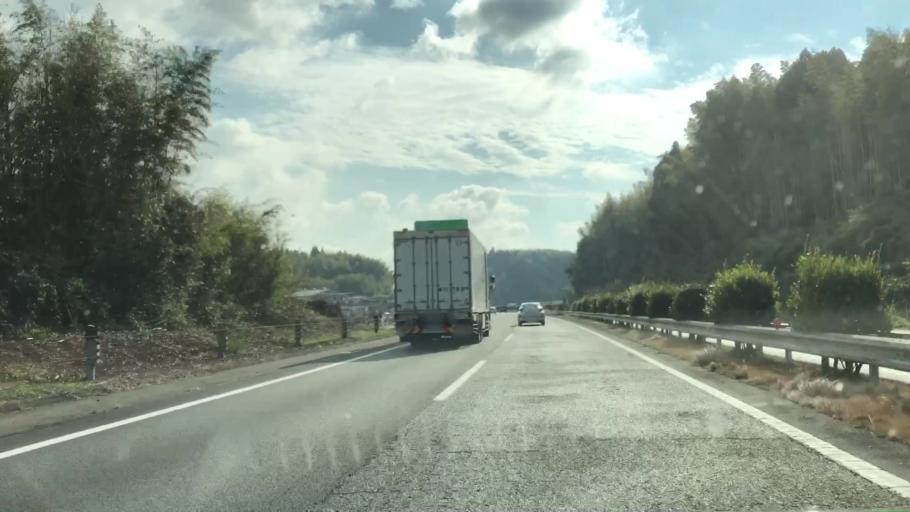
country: JP
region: Fukuoka
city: Setakamachi-takayanagi
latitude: 33.0818
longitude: 130.5416
